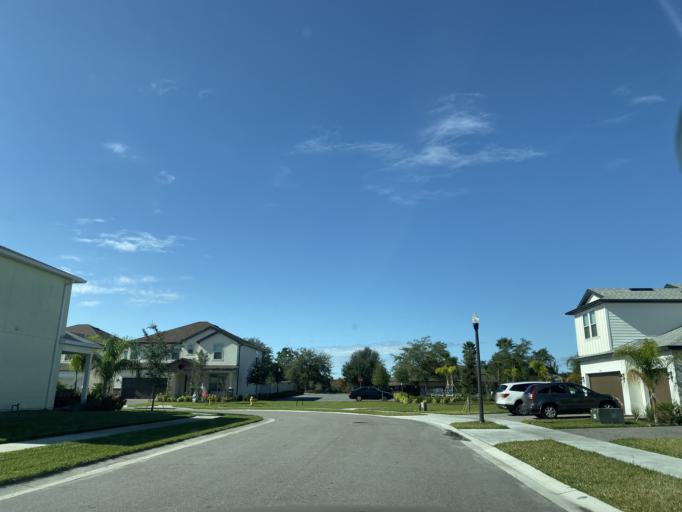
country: US
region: Florida
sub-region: Seminole County
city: Goldenrod
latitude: 28.6130
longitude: -81.2609
